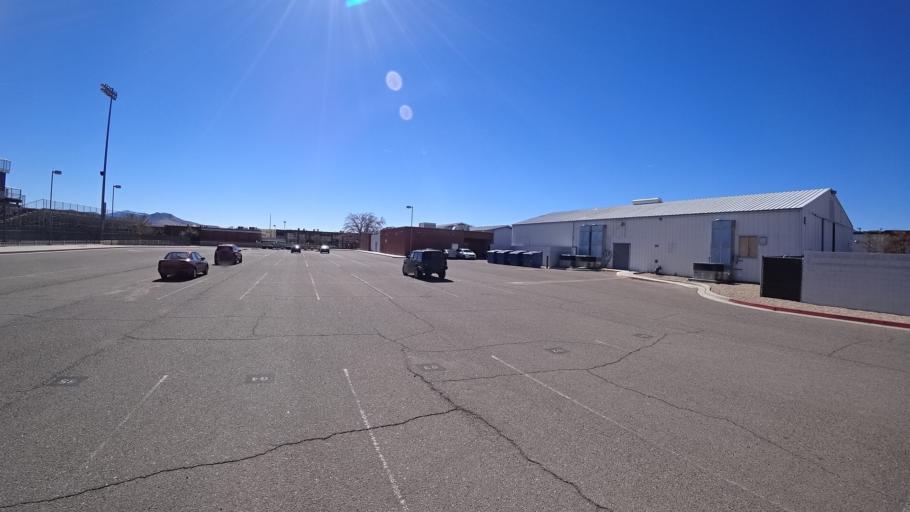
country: US
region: Arizona
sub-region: Mohave County
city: Kingman
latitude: 35.1934
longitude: -114.0598
